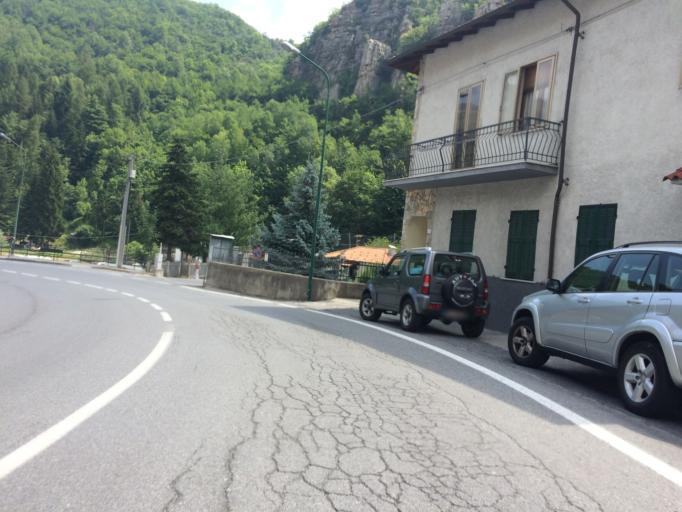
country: IT
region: Piedmont
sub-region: Provincia di Cuneo
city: Ormea
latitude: 44.1476
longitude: 7.9141
